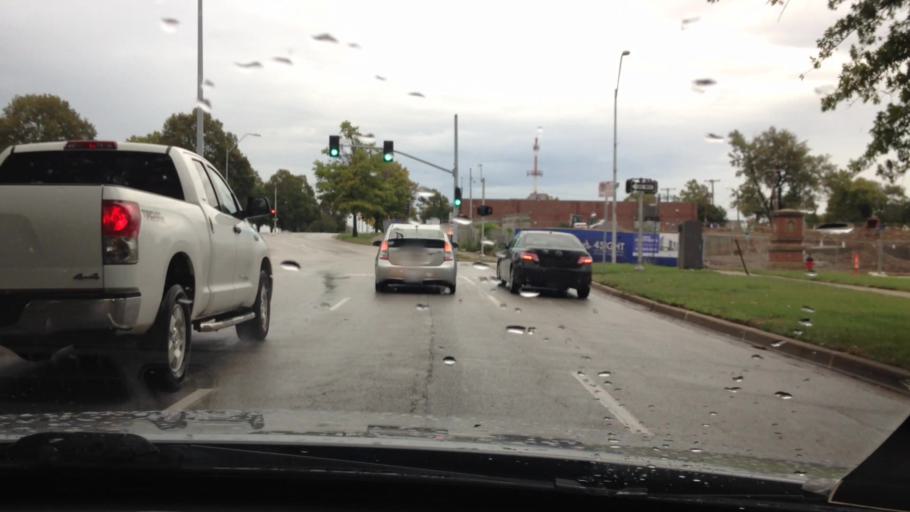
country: US
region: Missouri
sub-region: Jackson County
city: Kansas City
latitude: 39.1026
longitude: -94.5634
